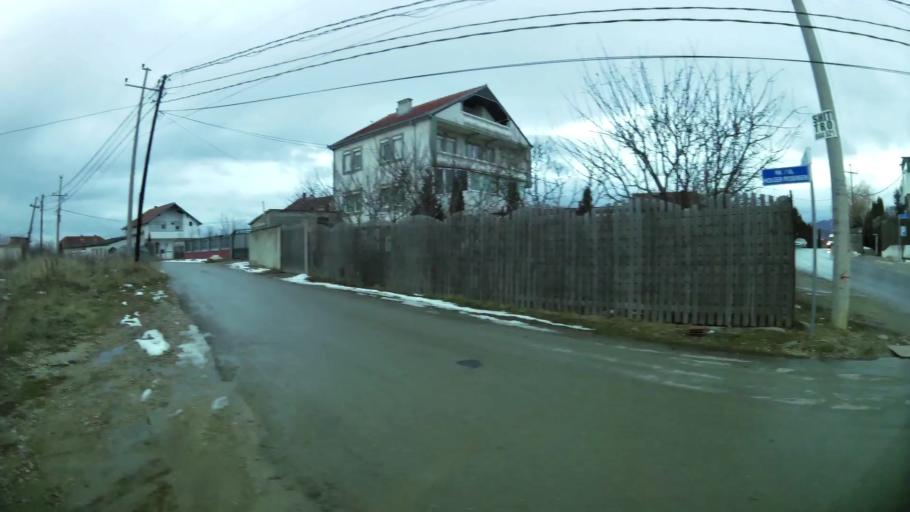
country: XK
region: Pristina
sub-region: Komuna e Prishtines
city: Pristina
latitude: 42.6304
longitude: 21.1616
